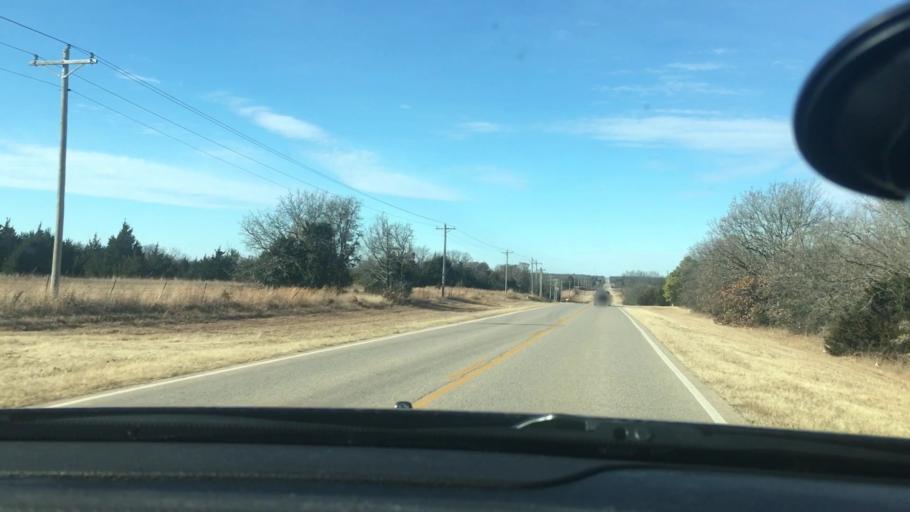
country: US
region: Oklahoma
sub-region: Cleveland County
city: Lexington
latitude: 35.0147
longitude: -97.1099
